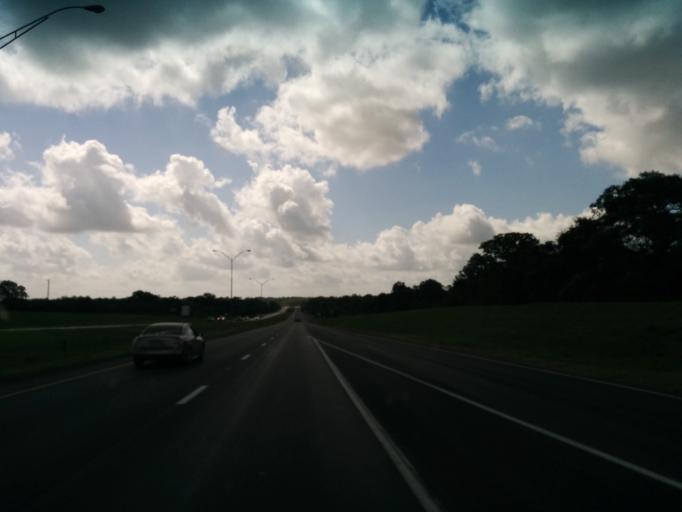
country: US
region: Texas
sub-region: Fayette County
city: Schulenburg
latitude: 29.6933
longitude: -96.8468
